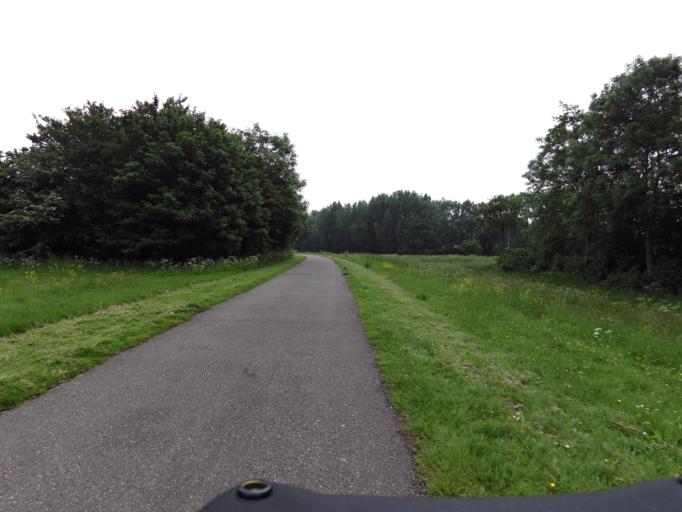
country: NL
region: South Holland
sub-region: Gemeente Spijkenisse
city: Spijkenisse
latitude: 51.8226
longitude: 4.2664
